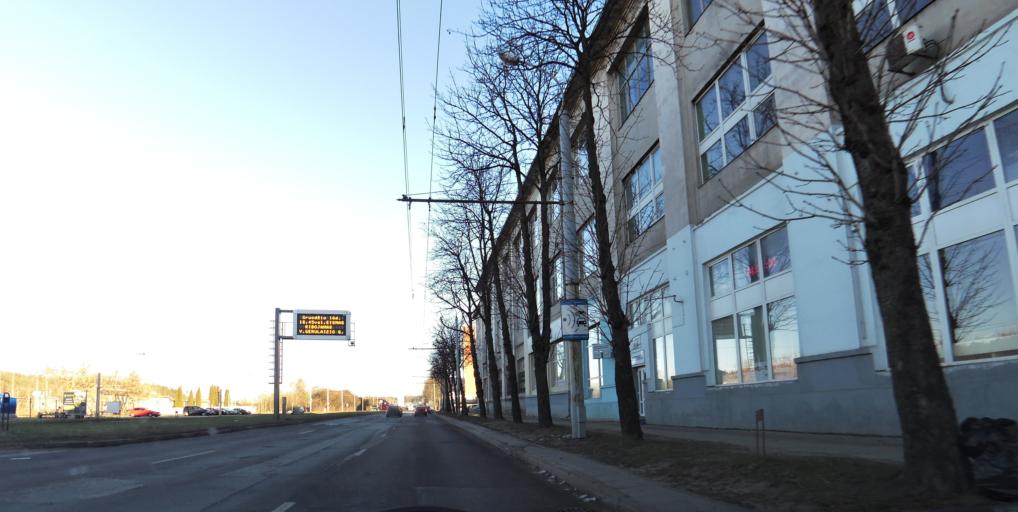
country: LT
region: Vilnius County
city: Lazdynai
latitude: 54.6508
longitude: 25.2184
